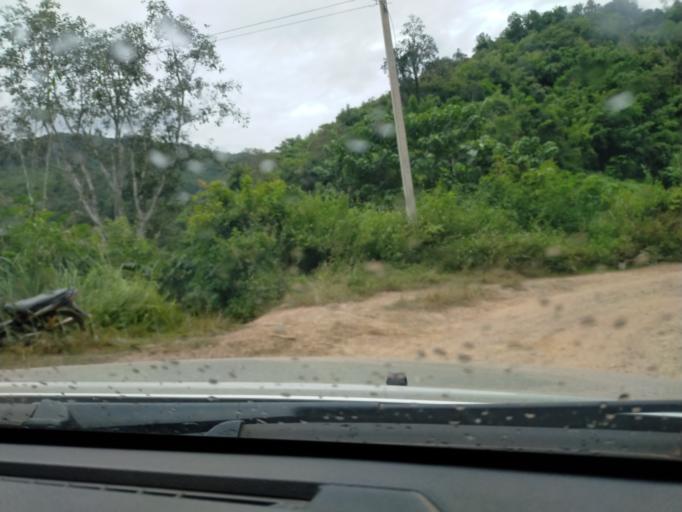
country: TH
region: Nan
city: Chaloem Phra Kiat
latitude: 19.8130
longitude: 101.3595
